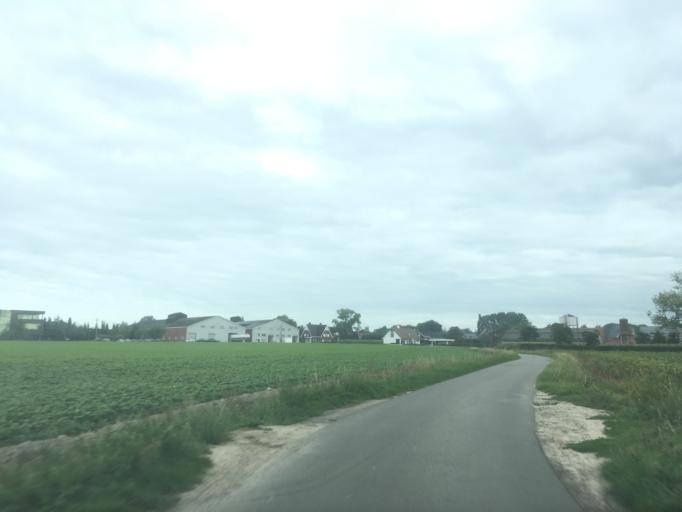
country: BE
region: Flanders
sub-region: Provincie West-Vlaanderen
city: Ardooie
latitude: 50.9971
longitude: 3.2027
